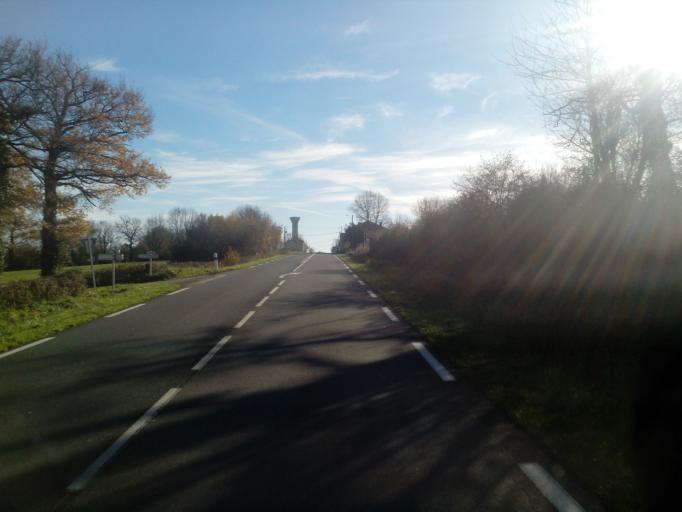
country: FR
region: Limousin
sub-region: Departement de la Haute-Vienne
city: Peyrat-de-Bellac
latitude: 46.1528
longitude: 0.9631
